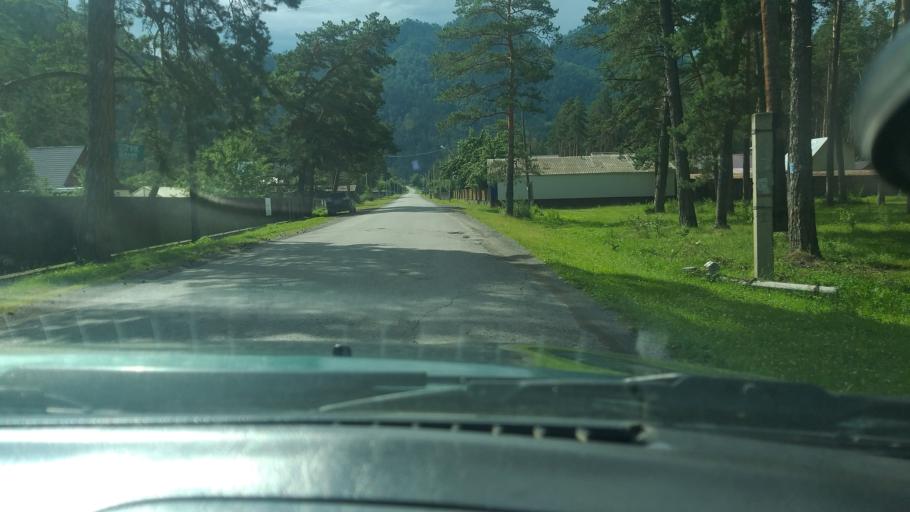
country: RU
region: Altay
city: Chemal
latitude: 51.3968
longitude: 86.0247
